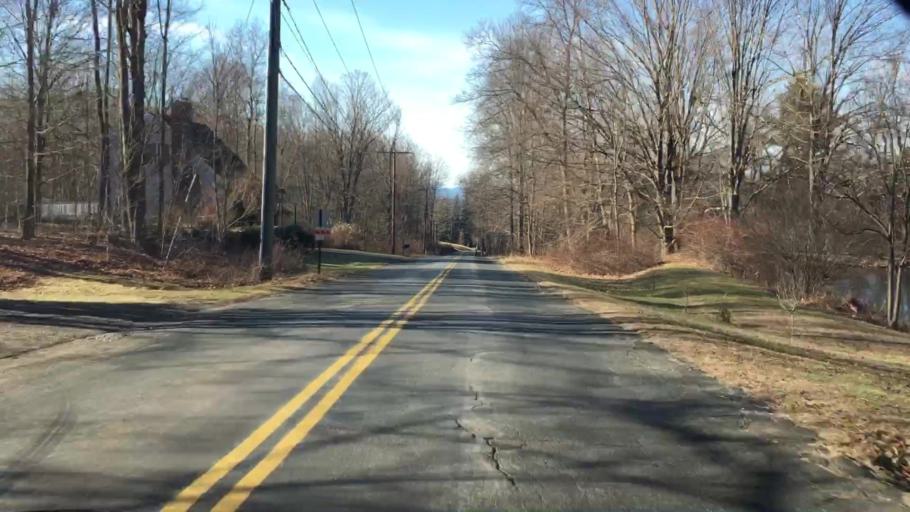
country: US
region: Connecticut
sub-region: Tolland County
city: Somers
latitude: 41.9690
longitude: -72.4324
